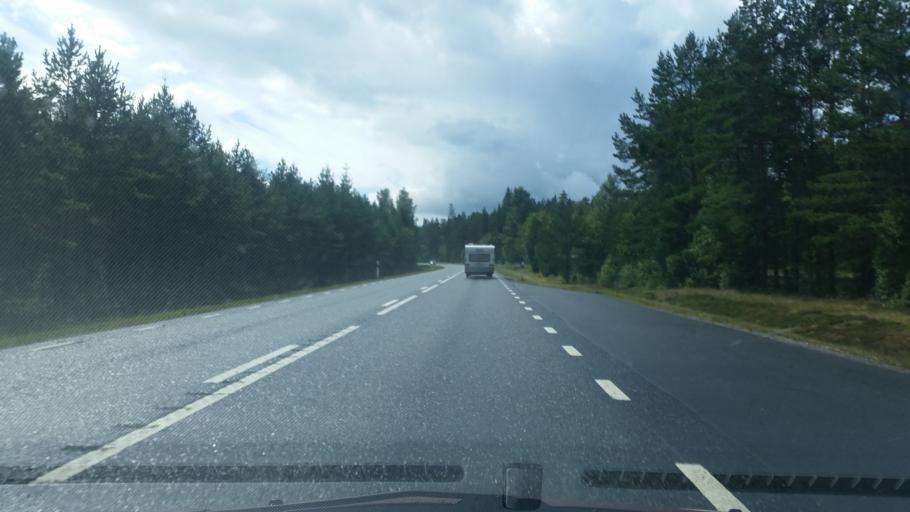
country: SE
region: Joenkoeping
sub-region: Gislaveds Kommun
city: Gislaved
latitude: 57.3820
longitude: 13.5808
